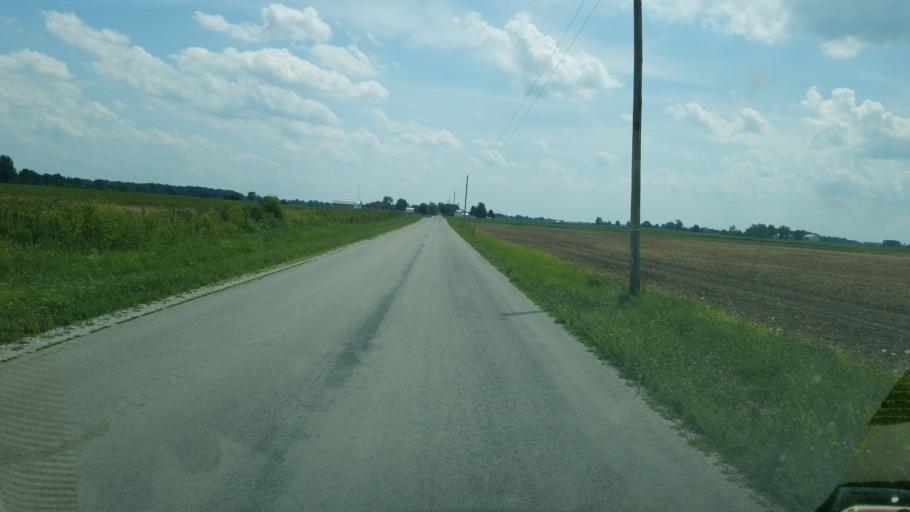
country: US
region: Ohio
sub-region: Hardin County
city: Forest
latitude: 40.8852
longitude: -83.4623
